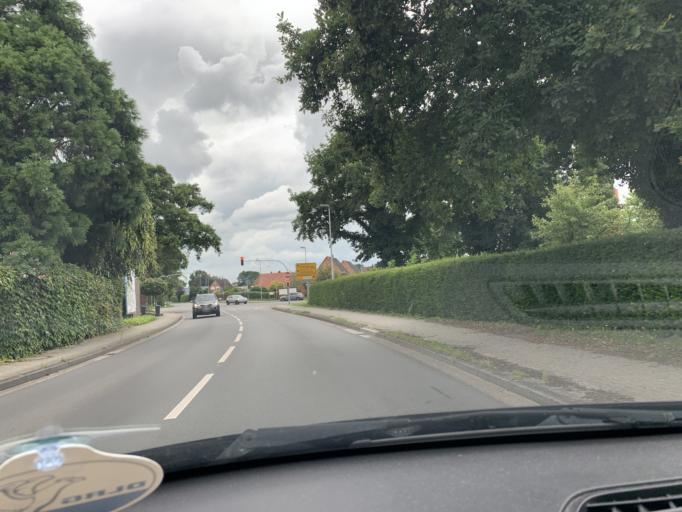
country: DE
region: Lower Saxony
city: Edewecht
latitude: 53.1164
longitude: 7.9689
